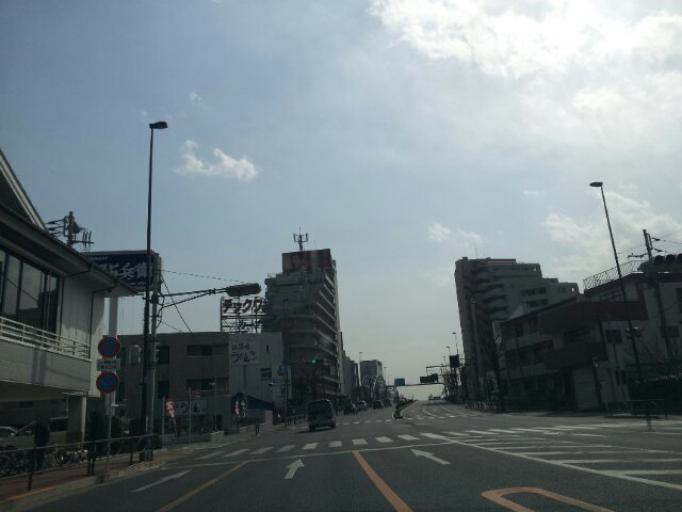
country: JP
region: Kanagawa
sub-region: Kawasaki-shi
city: Kawasaki
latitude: 35.5599
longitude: 139.6971
